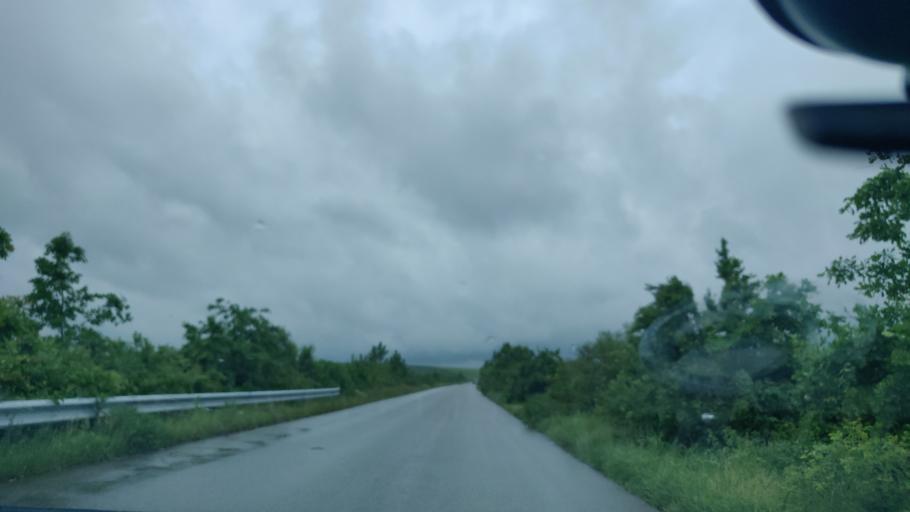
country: RO
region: Giurgiu
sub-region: Comuna Bulbucata
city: Bulbucata
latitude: 44.2926
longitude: 25.7689
